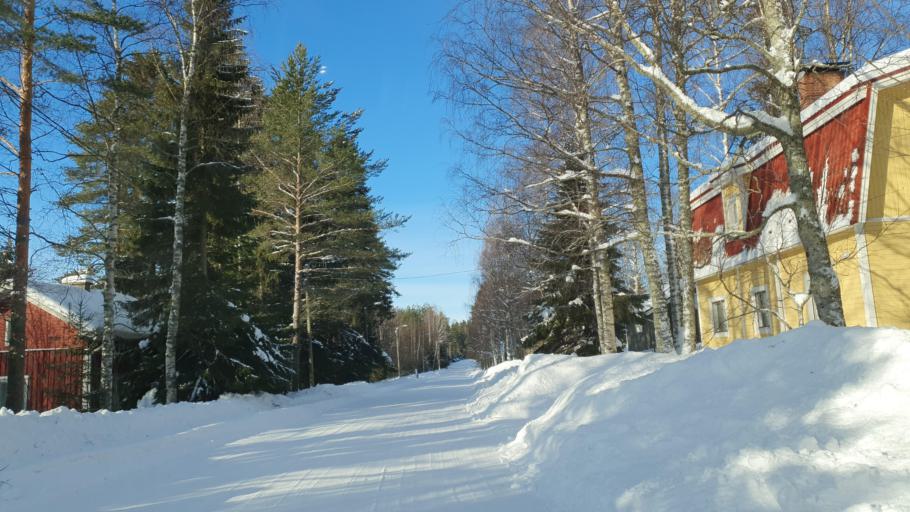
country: FI
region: Northern Ostrobothnia
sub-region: Oulu
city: Haukipudas
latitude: 65.1922
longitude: 25.4235
